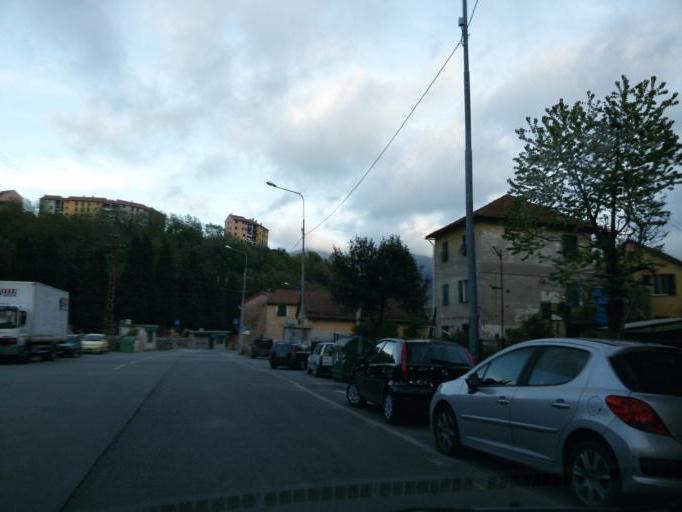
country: IT
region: Liguria
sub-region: Provincia di Genova
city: Santa Marta
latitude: 44.4721
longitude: 8.8931
